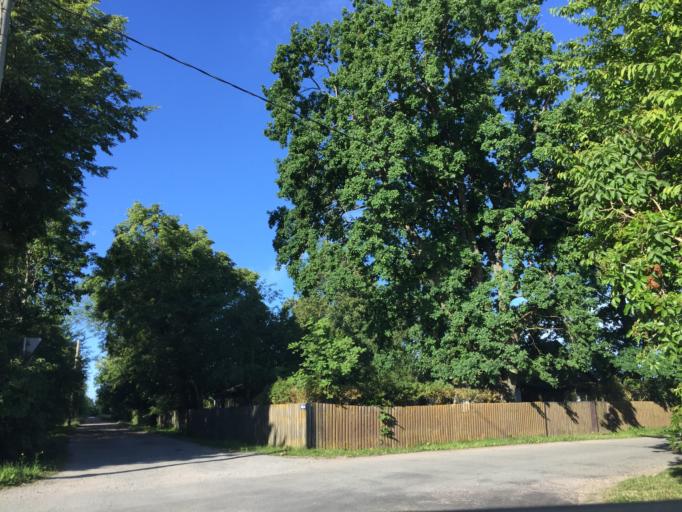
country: LV
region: Ventspils
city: Ventspils
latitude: 57.3663
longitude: 21.6060
